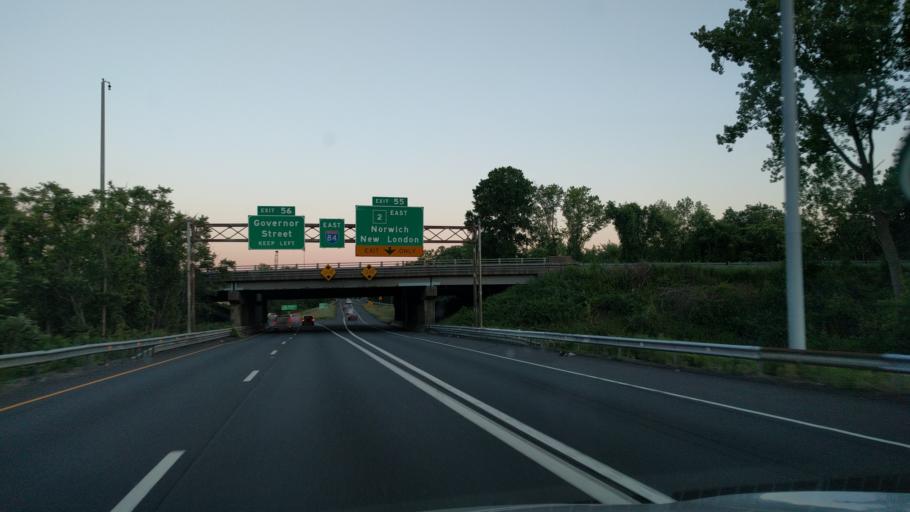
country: US
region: Connecticut
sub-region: Hartford County
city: Hartford
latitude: 41.7674
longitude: -72.6580
